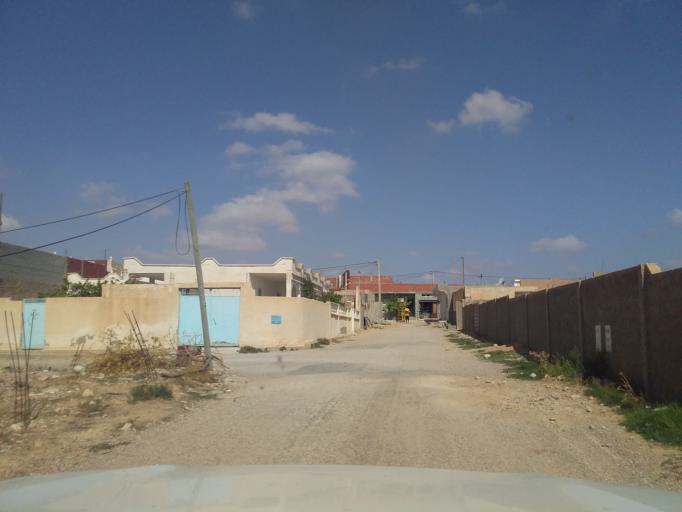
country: TN
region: Madanin
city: Medenine
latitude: 33.5848
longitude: 10.3243
